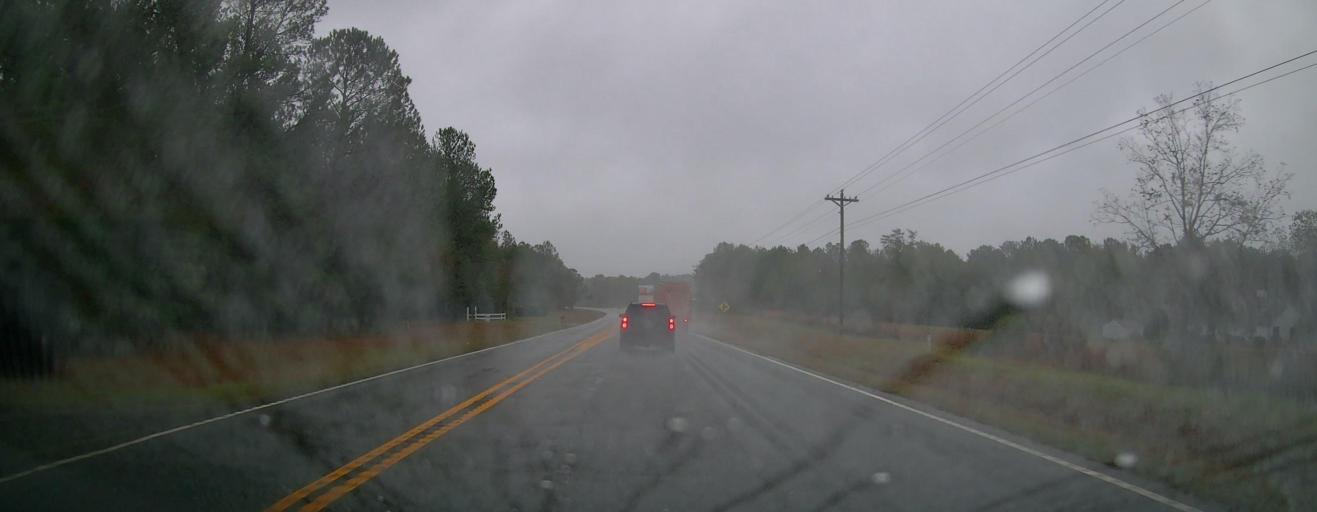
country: US
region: Georgia
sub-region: Jones County
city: Gray
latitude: 33.0740
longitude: -83.4856
